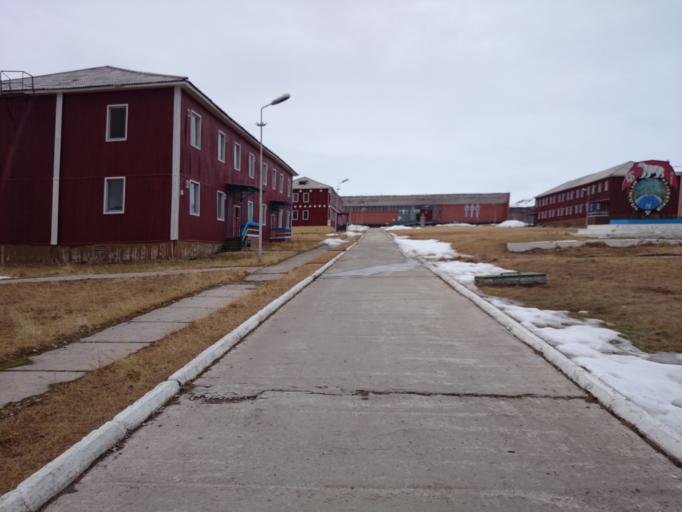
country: SJ
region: Svalbard
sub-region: Spitsbergen
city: Longyearbyen
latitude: 78.6556
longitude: 16.3173
